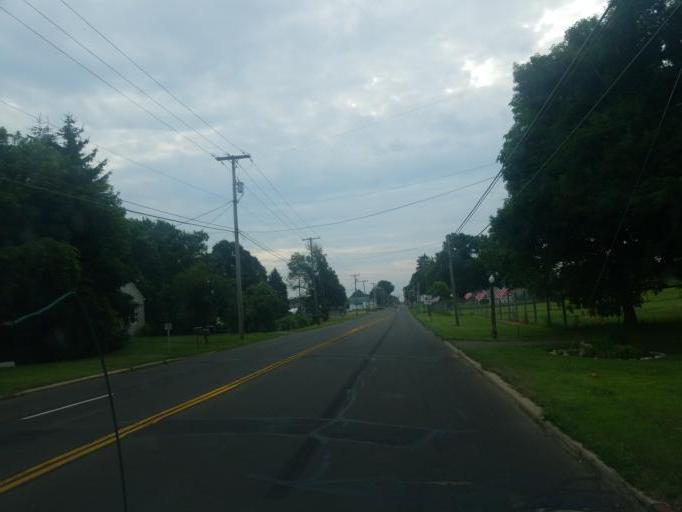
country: US
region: Ohio
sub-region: Stark County
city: Massillon
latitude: 40.7985
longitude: -81.6057
